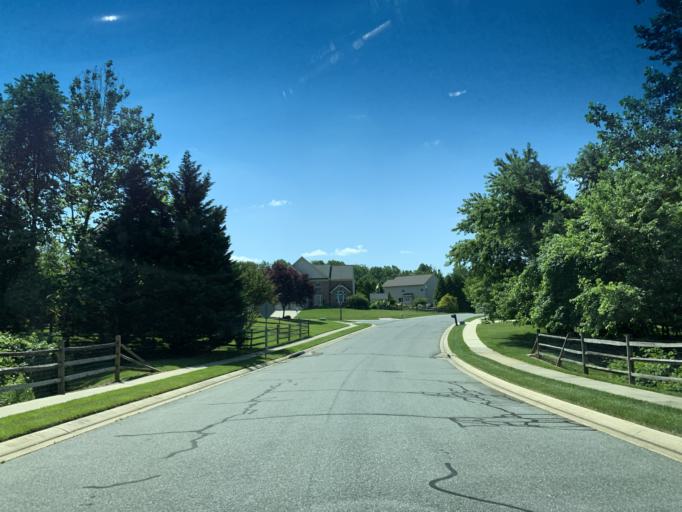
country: US
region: Maryland
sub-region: Harford County
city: South Bel Air
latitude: 39.5185
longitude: -76.3424
